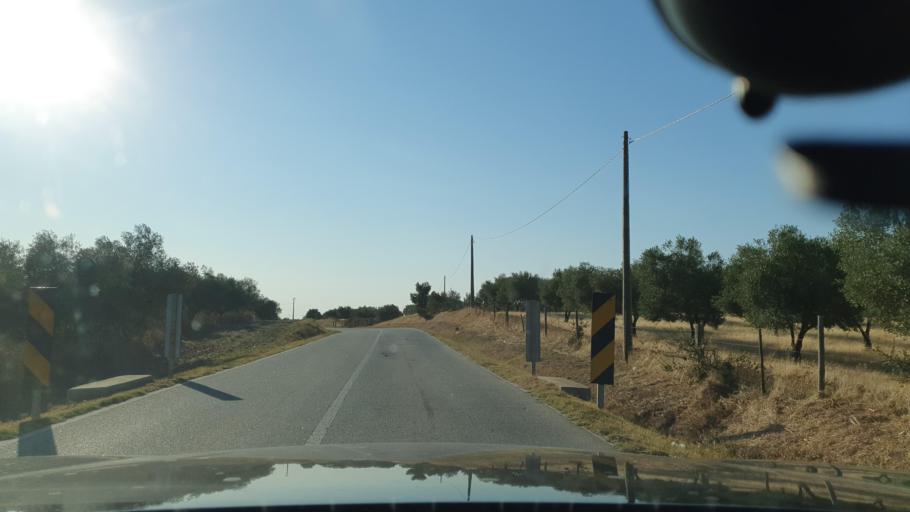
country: PT
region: Evora
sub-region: Estremoz
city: Estremoz
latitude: 38.8902
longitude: -7.6562
